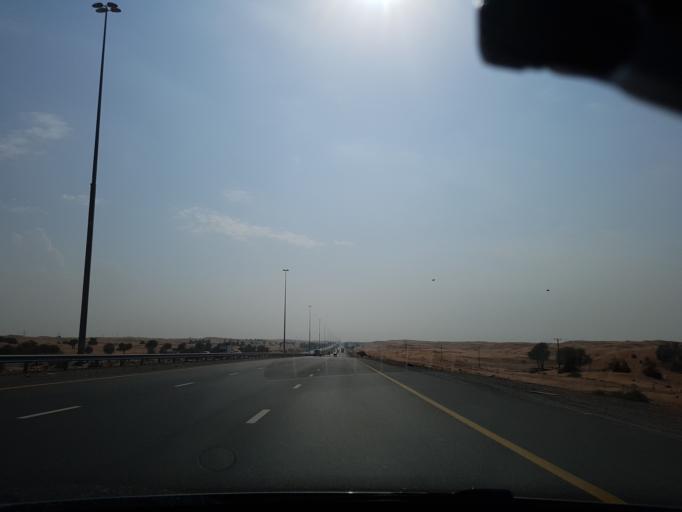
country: AE
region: Umm al Qaywayn
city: Umm al Qaywayn
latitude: 25.5177
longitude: 55.7112
